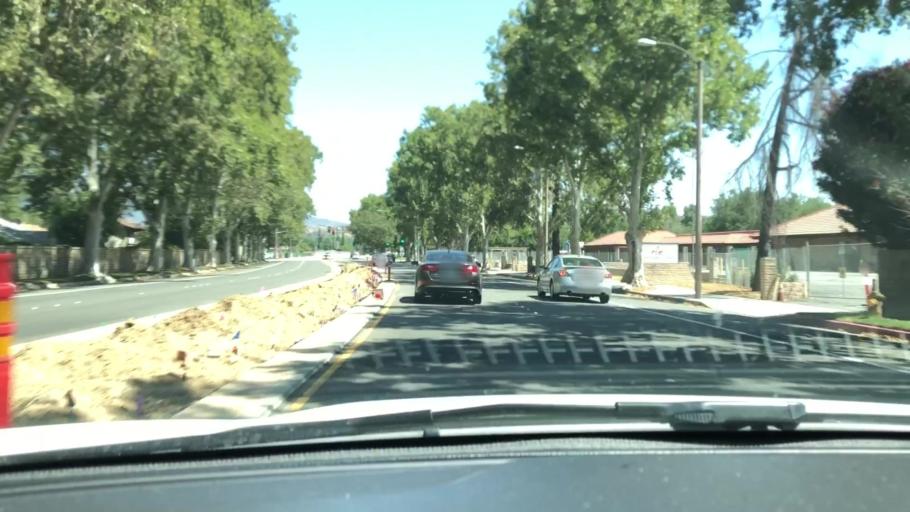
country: US
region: California
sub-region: Los Angeles County
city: Santa Clarita
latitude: 34.3911
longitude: -118.5490
